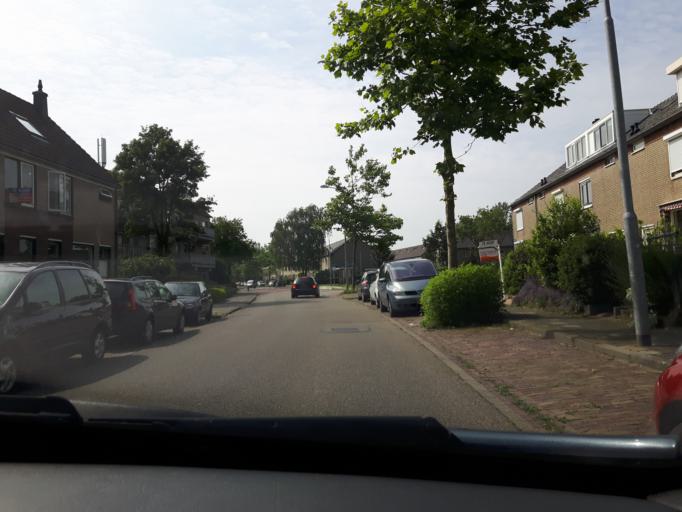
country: NL
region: Zeeland
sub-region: Gemeente Middelburg
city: Middelburg
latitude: 51.4821
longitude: 3.6193
